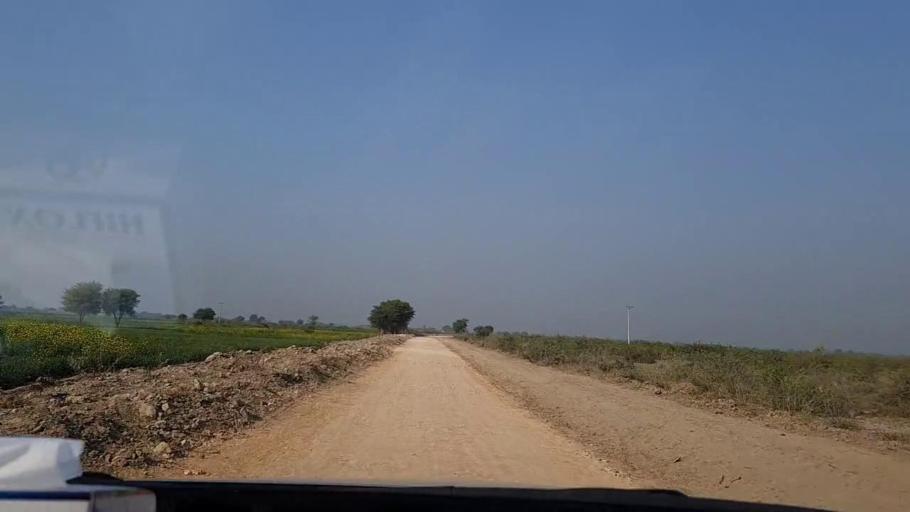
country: PK
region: Sindh
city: Tando Ghulam Ali
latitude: 25.1509
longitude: 68.8757
